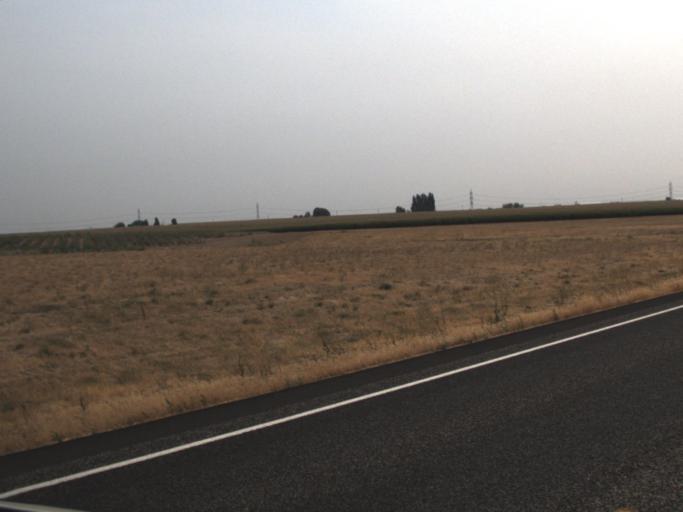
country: US
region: Washington
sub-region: Benton County
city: Benton City
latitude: 46.1121
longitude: -119.6018
